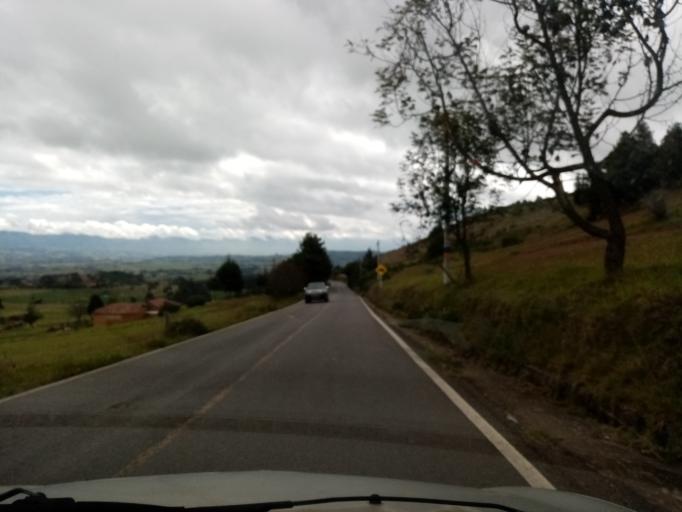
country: CO
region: Boyaca
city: Siachoque
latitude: 5.5680
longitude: -73.2755
